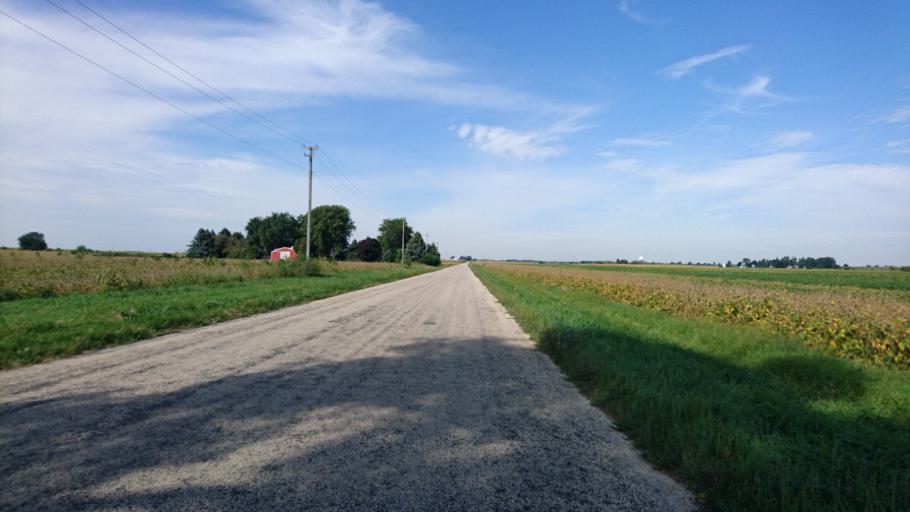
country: US
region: Illinois
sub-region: Will County
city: Manhattan
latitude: 41.4167
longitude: -88.0268
